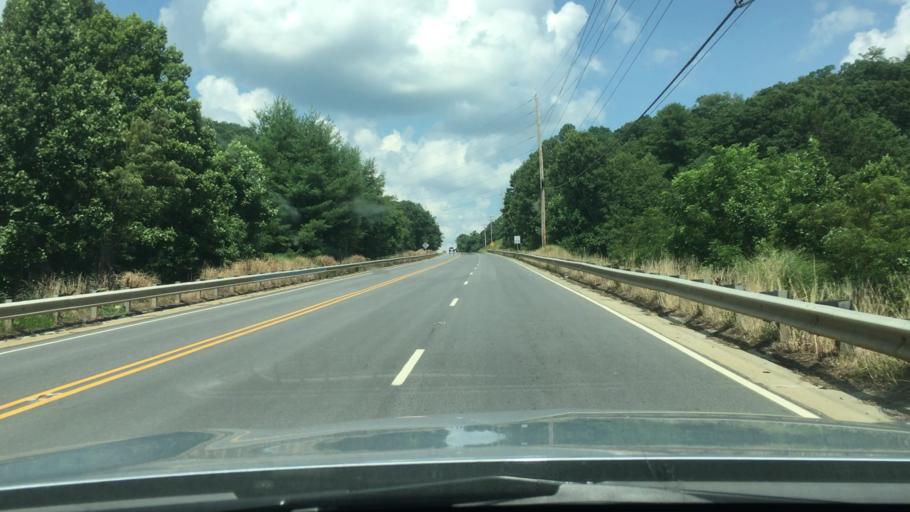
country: US
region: North Carolina
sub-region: Madison County
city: Marshall
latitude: 35.8200
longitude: -82.6395
